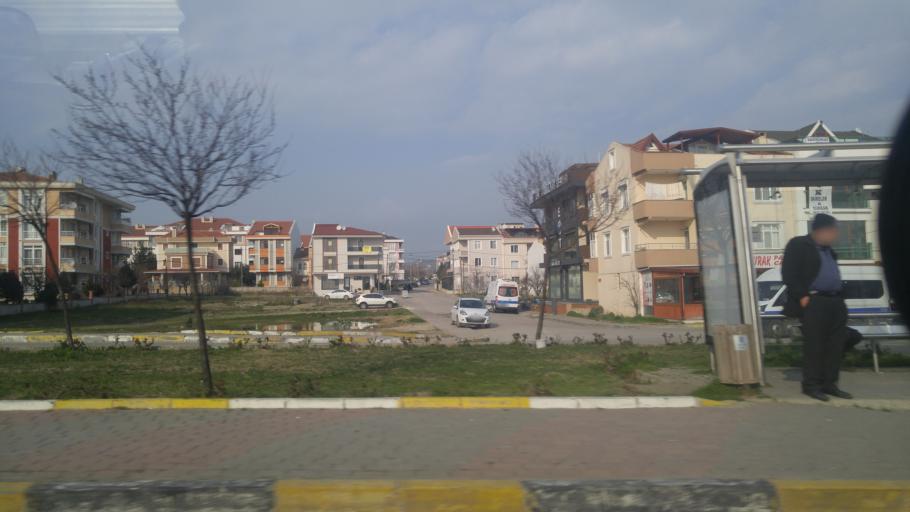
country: TR
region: Istanbul
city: Selimpasa
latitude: 41.0546
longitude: 28.3757
